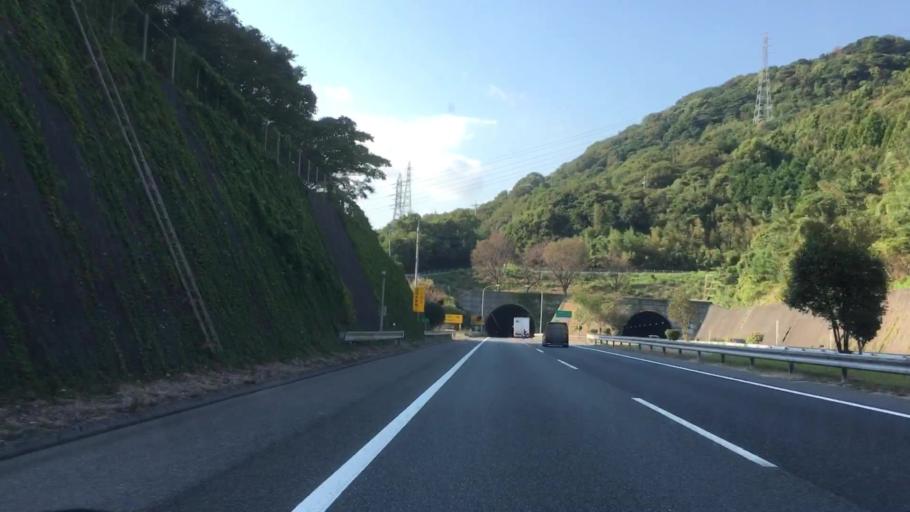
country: JP
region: Yamaguchi
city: Tokuyama
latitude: 34.0597
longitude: 131.8365
